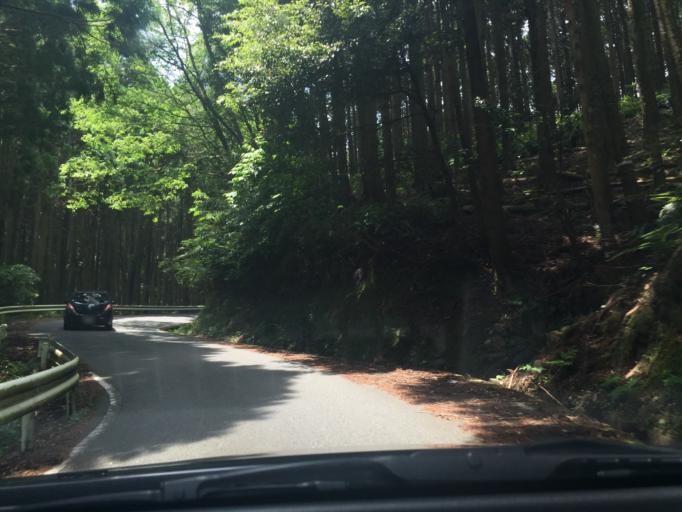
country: JP
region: Shizuoka
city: Shimoda
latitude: 34.7066
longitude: 138.8028
